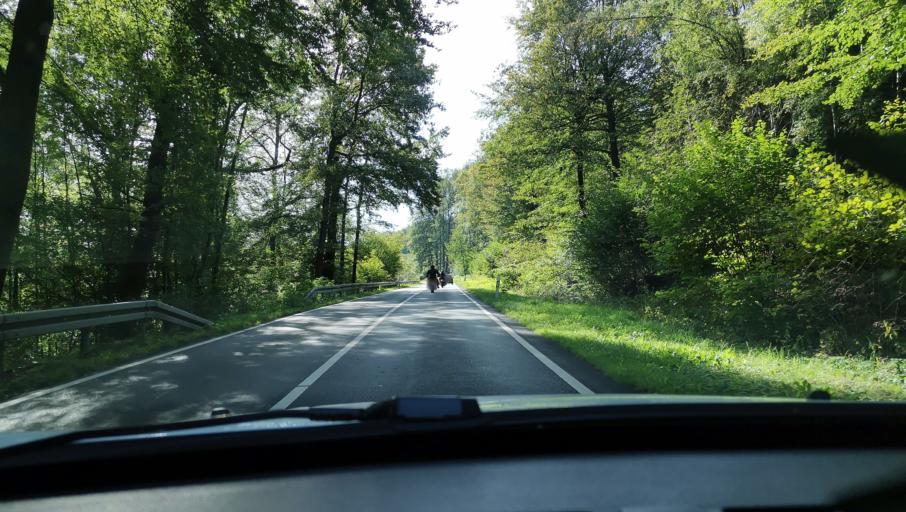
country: DE
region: North Rhine-Westphalia
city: Kierspe
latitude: 51.1172
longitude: 7.6175
